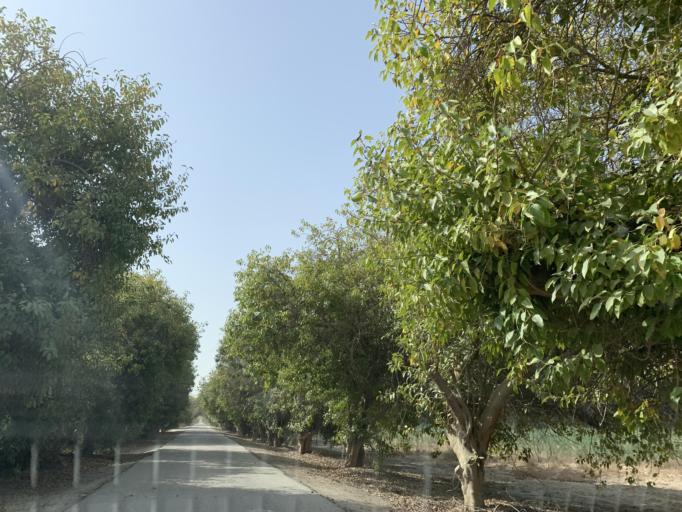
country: BH
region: Northern
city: Madinat `Isa
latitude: 26.1658
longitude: 50.5300
